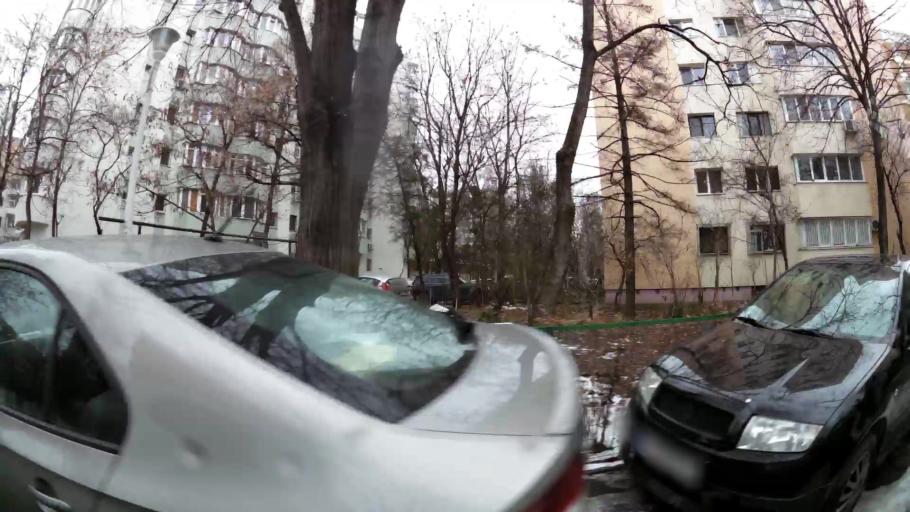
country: RO
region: Ilfov
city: Dobroesti
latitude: 44.4319
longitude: 26.1649
